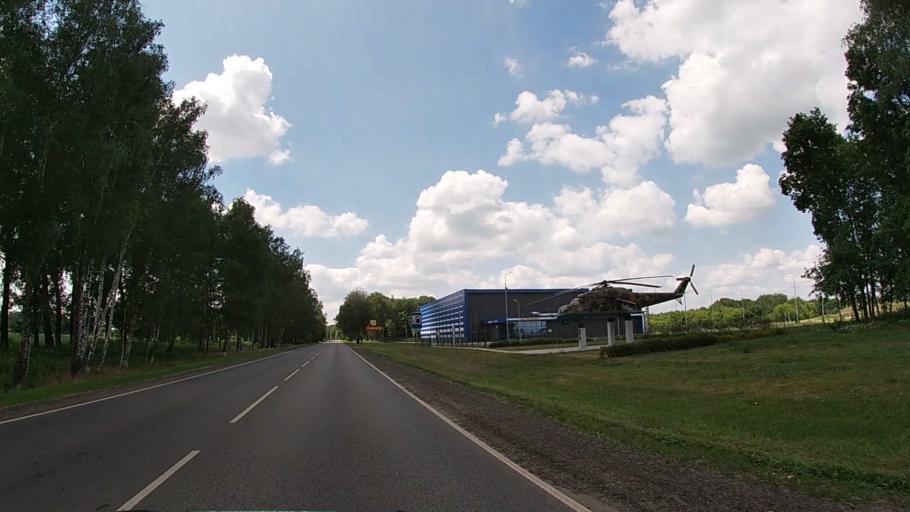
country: RU
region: Belgorod
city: Grayvoron
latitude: 50.4928
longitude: 35.7033
